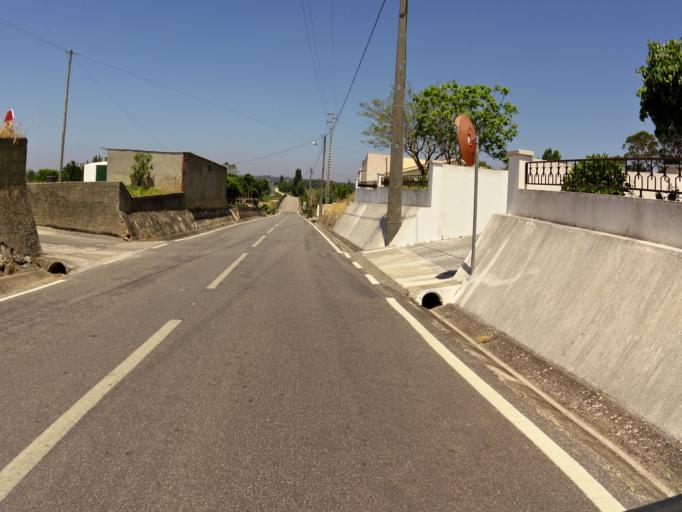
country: PT
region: Coimbra
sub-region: Montemor-O-Velho
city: Montemor-o-Velho
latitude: 40.1586
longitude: -8.7136
